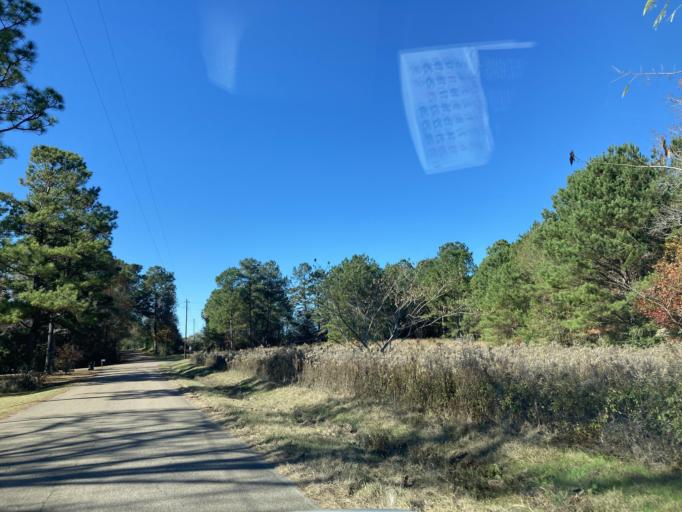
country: US
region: Mississippi
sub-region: Lamar County
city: Sumrall
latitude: 31.3113
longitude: -89.6151
